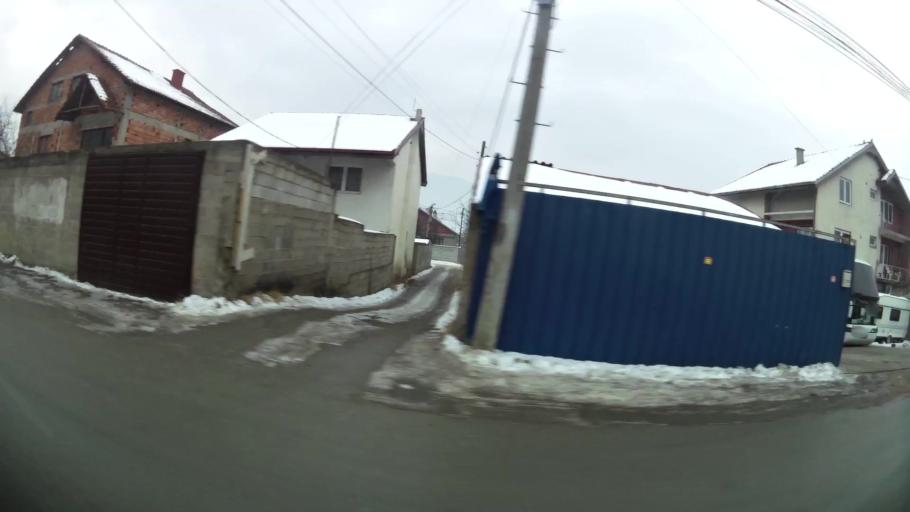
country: MK
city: Kondovo
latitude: 42.0100
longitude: 21.3218
